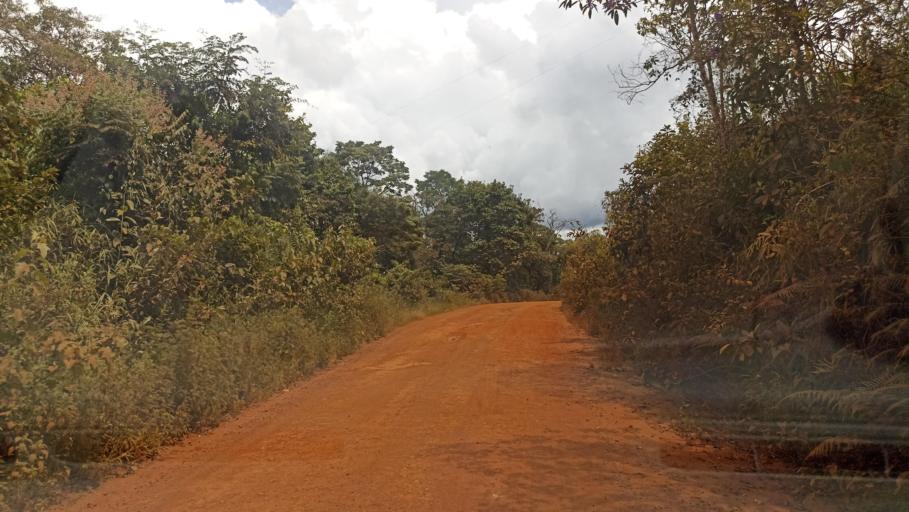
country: BR
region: Minas Gerais
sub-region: Itabirito
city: Itabirito
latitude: -20.3451
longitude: -43.7486
